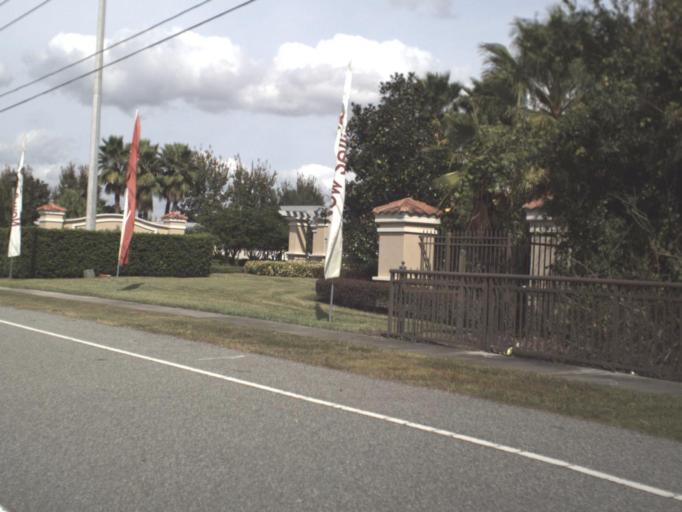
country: US
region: Florida
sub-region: Osceola County
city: Poinciana
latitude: 28.1707
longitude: -81.4481
